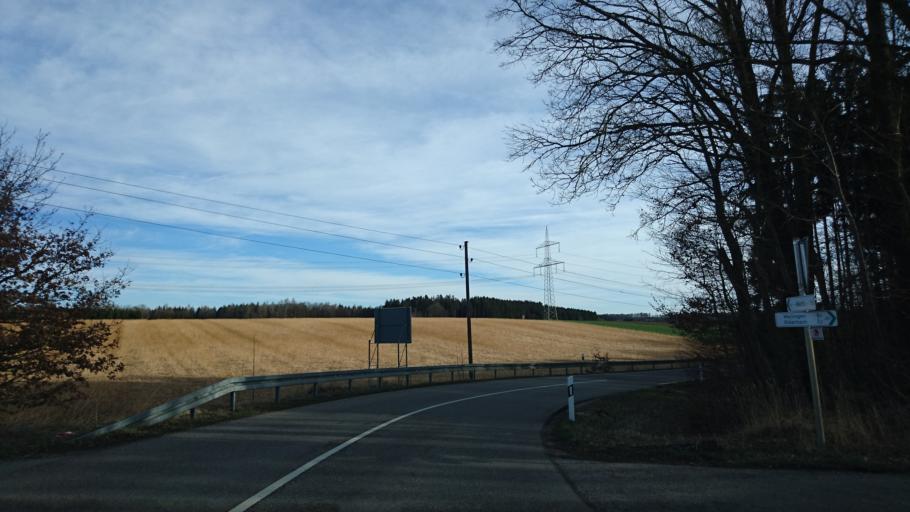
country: DE
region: Bavaria
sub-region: Swabia
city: Biberbach
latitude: 48.5254
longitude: 10.7861
